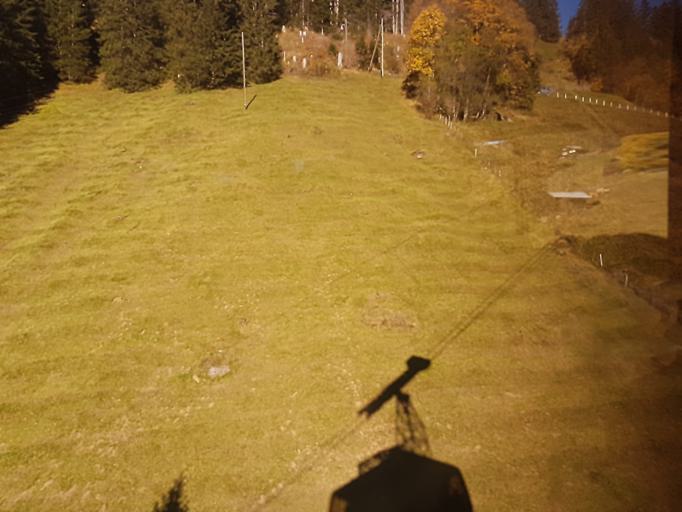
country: CH
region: Bern
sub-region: Interlaken-Oberhasli District
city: Lauterbrunnen
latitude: 46.5527
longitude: 7.8920
